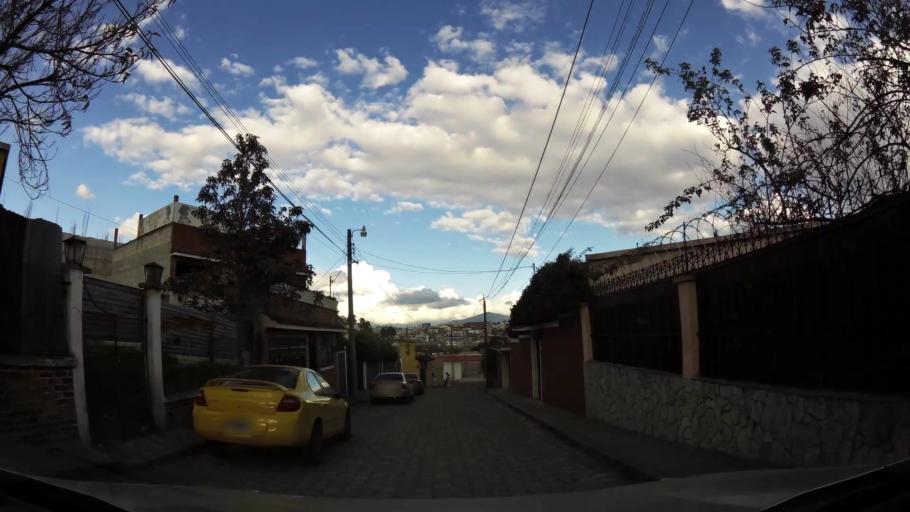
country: GT
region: Quetzaltenango
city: Quetzaltenango
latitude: 14.8532
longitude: -91.5267
